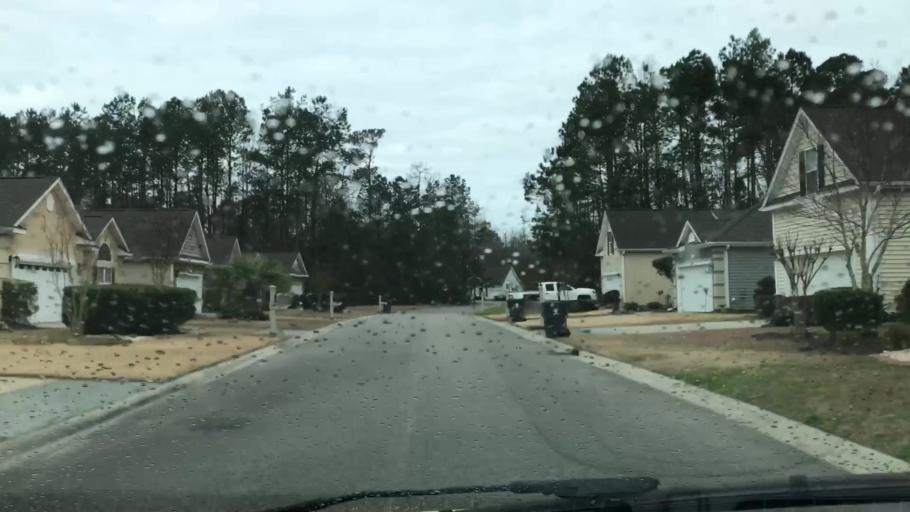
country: US
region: South Carolina
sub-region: Horry County
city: Red Hill
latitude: 33.7770
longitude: -79.0081
